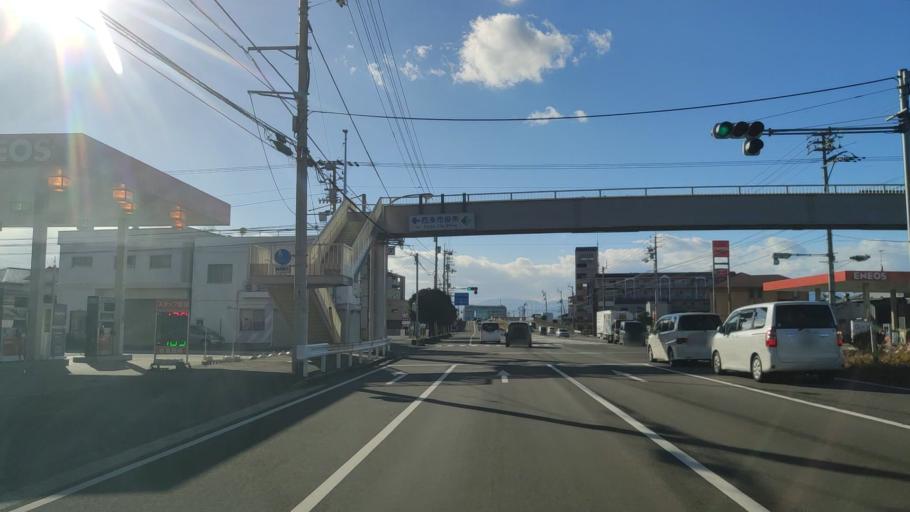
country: JP
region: Ehime
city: Saijo
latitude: 33.9271
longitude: 133.1788
